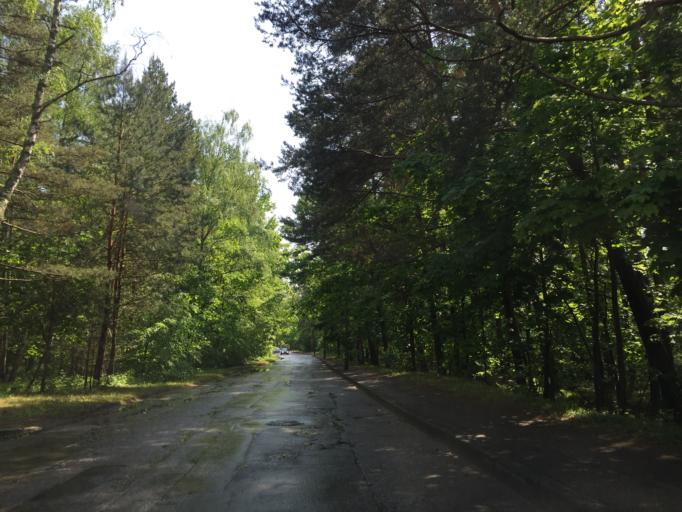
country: LT
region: Klaipedos apskritis
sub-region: Klaipeda
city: Klaipeda
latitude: 55.7710
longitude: 21.0836
